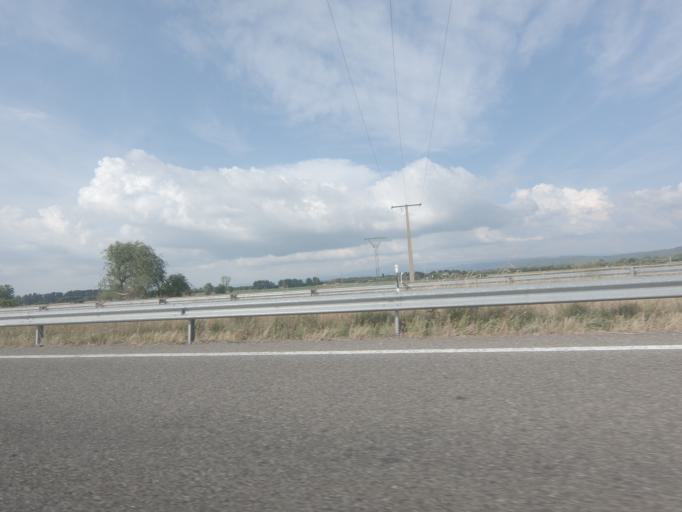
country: ES
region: Galicia
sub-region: Provincia de Ourense
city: Xinzo de Limia
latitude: 42.0918
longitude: -7.7236
